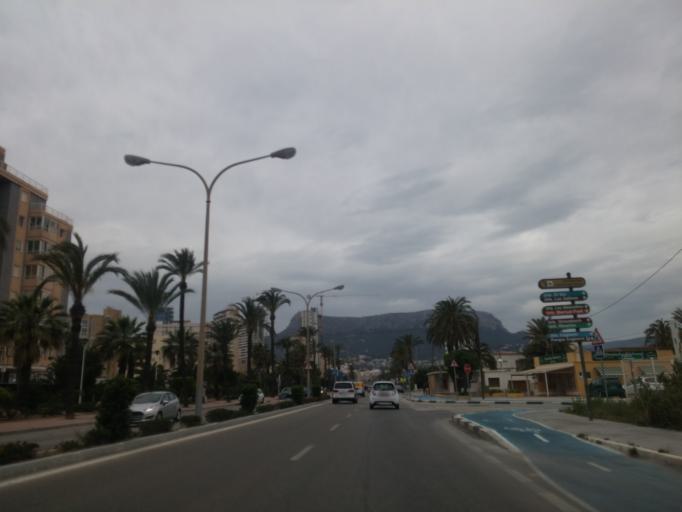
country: ES
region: Valencia
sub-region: Provincia de Alicante
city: Calp
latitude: 38.6426
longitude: 0.0625
